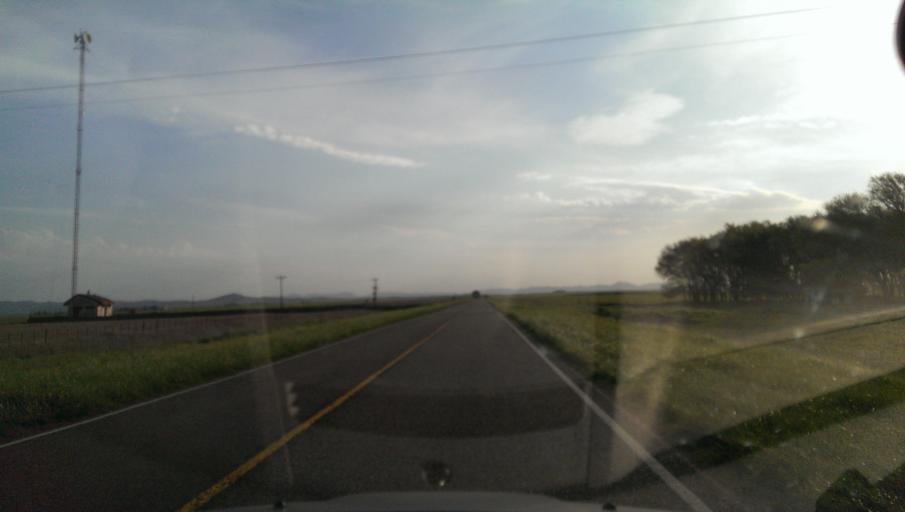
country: AR
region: Buenos Aires
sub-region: Partido de Coronel Suarez
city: Coronel Suarez
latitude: -37.7758
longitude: -61.7150
